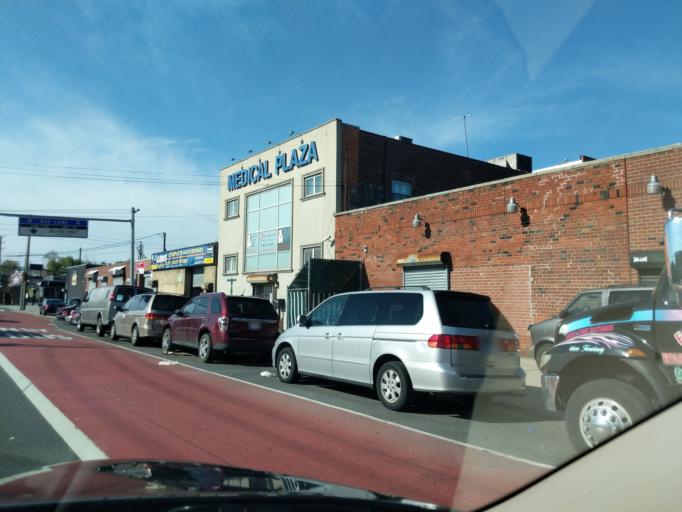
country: US
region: New York
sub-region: Kings County
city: Brooklyn
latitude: 40.6383
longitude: -73.9289
